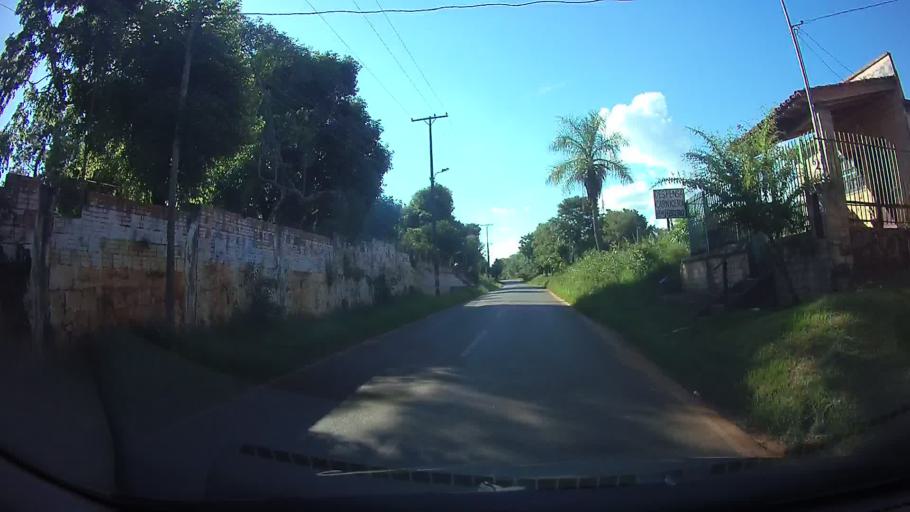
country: PY
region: Central
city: Itaugua
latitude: -25.3635
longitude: -57.3761
